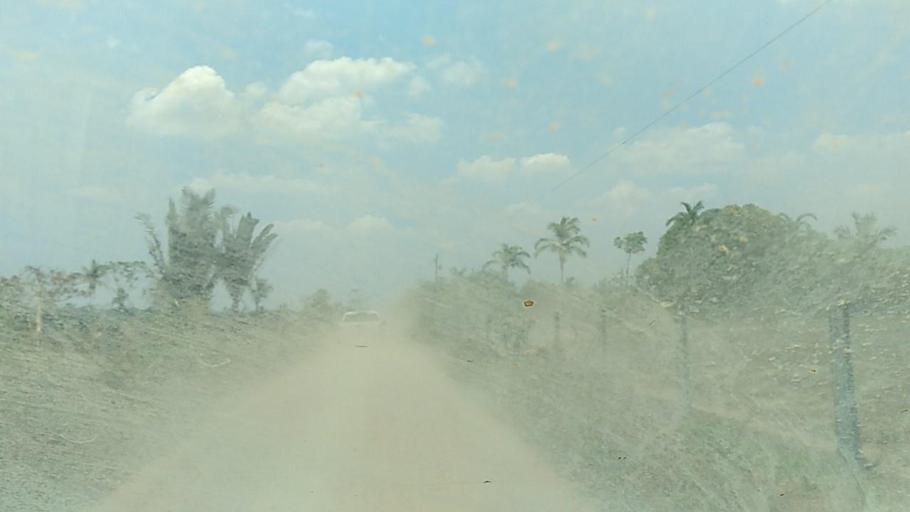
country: BR
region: Rondonia
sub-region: Porto Velho
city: Porto Velho
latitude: -8.7294
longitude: -63.3096
